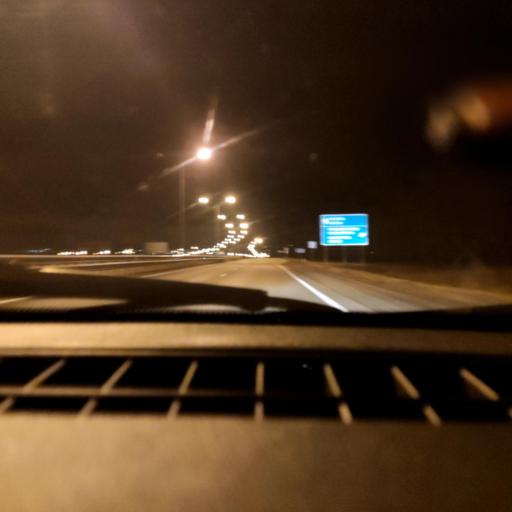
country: RU
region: Bashkortostan
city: Kushnarenkovo
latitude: 55.0546
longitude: 55.4352
